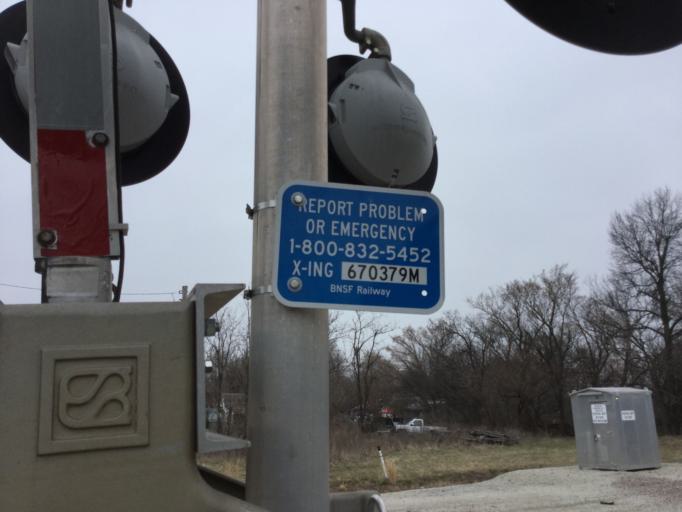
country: US
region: Kansas
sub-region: Cherokee County
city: Baxter Springs
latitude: 37.0210
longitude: -94.7437
